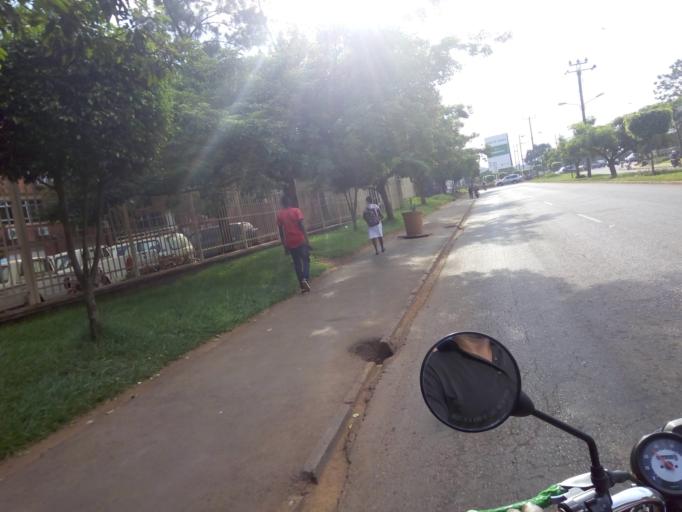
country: UG
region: Central Region
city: Kampala Central Division
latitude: 0.3330
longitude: 32.5779
